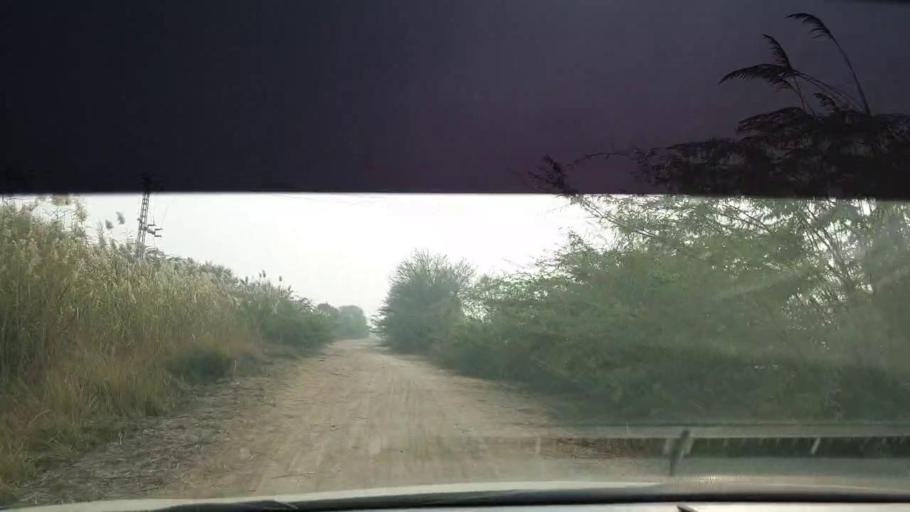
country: PK
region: Sindh
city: Berani
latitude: 25.8242
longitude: 68.8355
